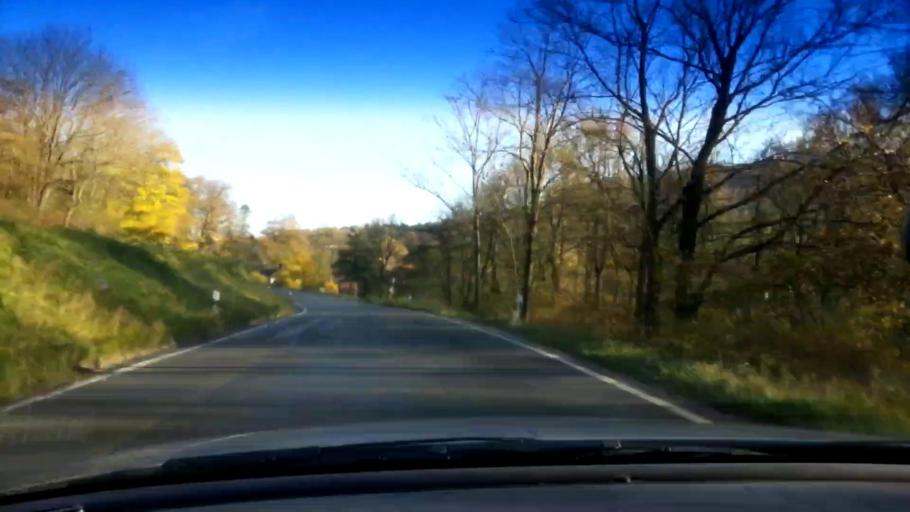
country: DE
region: Bavaria
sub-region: Upper Franconia
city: Heiligenstadt
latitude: 49.8775
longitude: 11.1362
